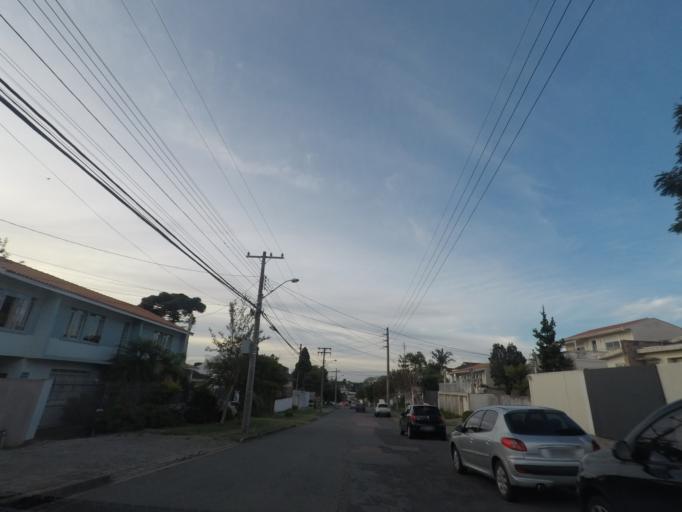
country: BR
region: Parana
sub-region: Curitiba
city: Curitiba
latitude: -25.4196
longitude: -49.2842
